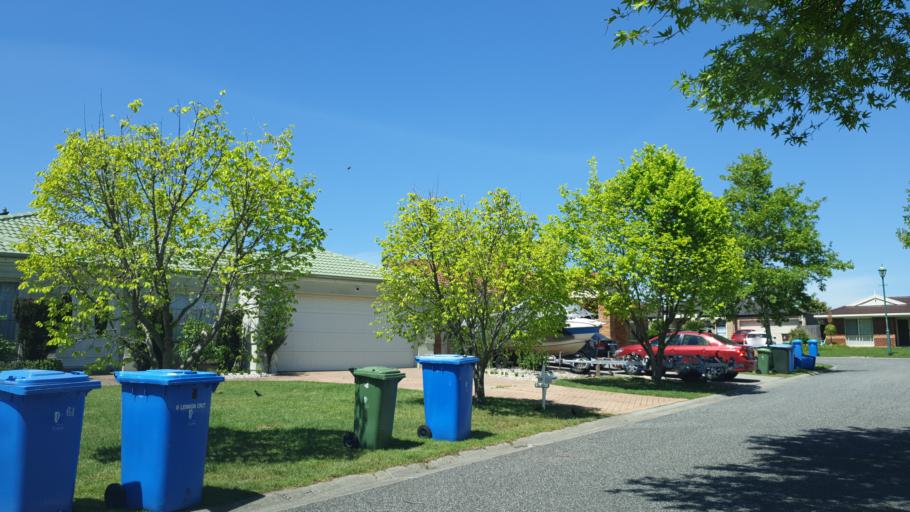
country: AU
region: Victoria
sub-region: Casey
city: Narre Warren South
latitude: -38.0657
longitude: 145.2963
